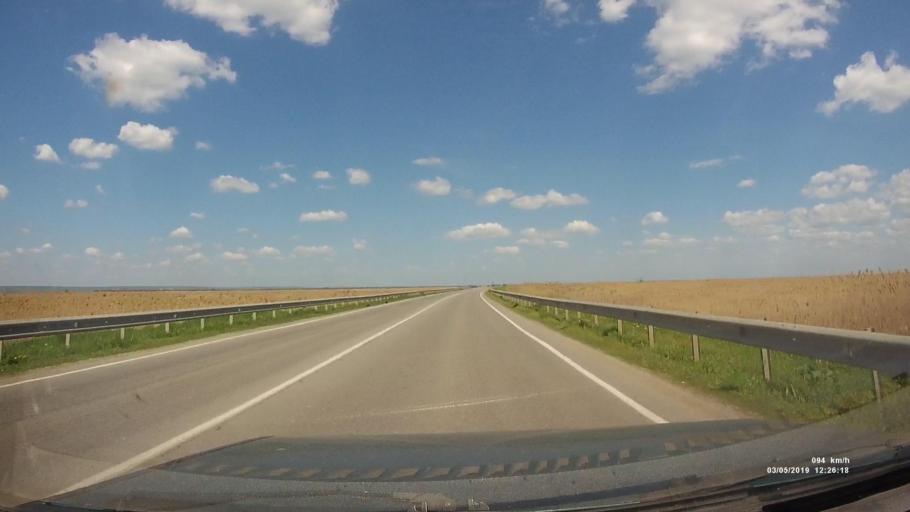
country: RU
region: Rostov
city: Semikarakorsk
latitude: 47.4433
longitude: 40.7128
